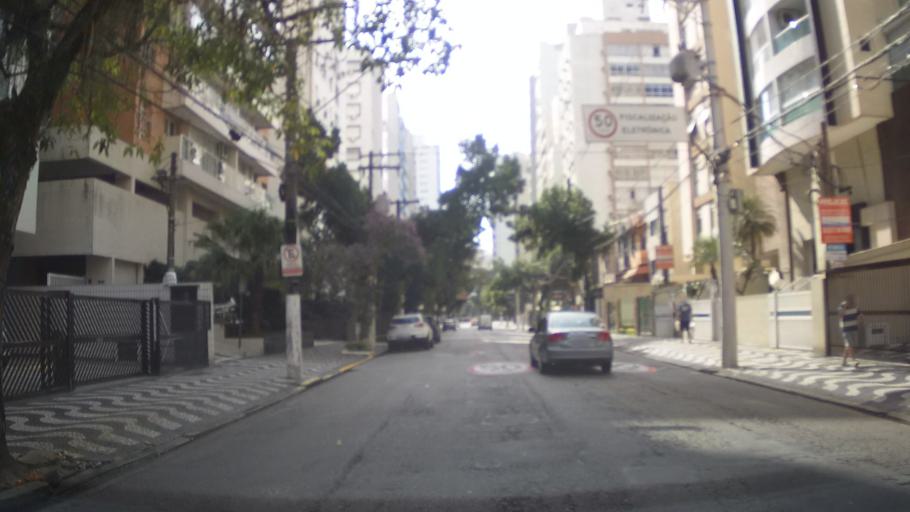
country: BR
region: Sao Paulo
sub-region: Santos
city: Santos
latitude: -23.9676
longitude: -46.3309
